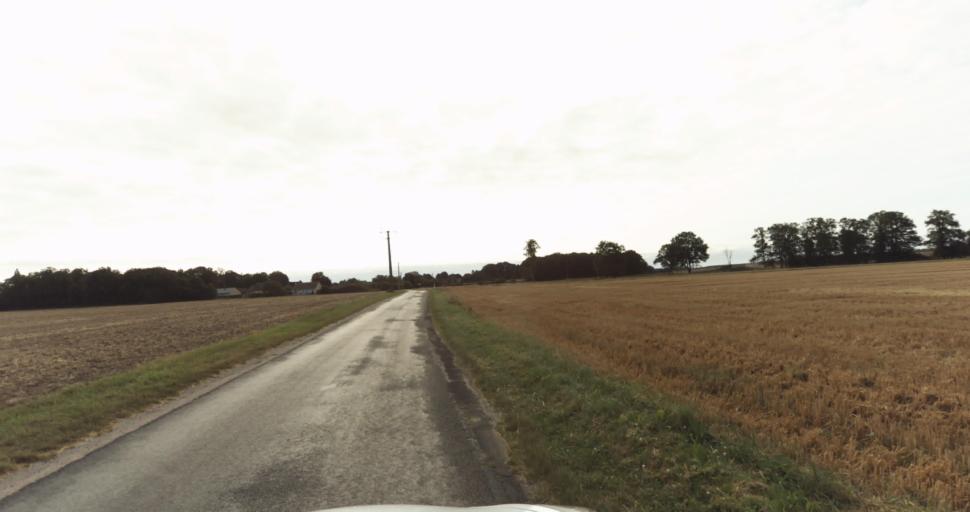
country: FR
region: Haute-Normandie
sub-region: Departement de l'Eure
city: Nonancourt
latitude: 48.8418
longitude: 1.1572
